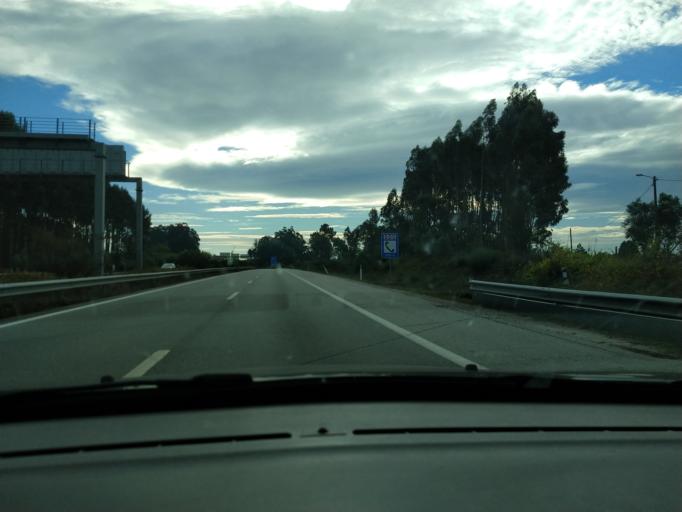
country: PT
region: Aveiro
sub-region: Estarreja
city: Salreu
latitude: 40.6846
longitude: -8.5380
